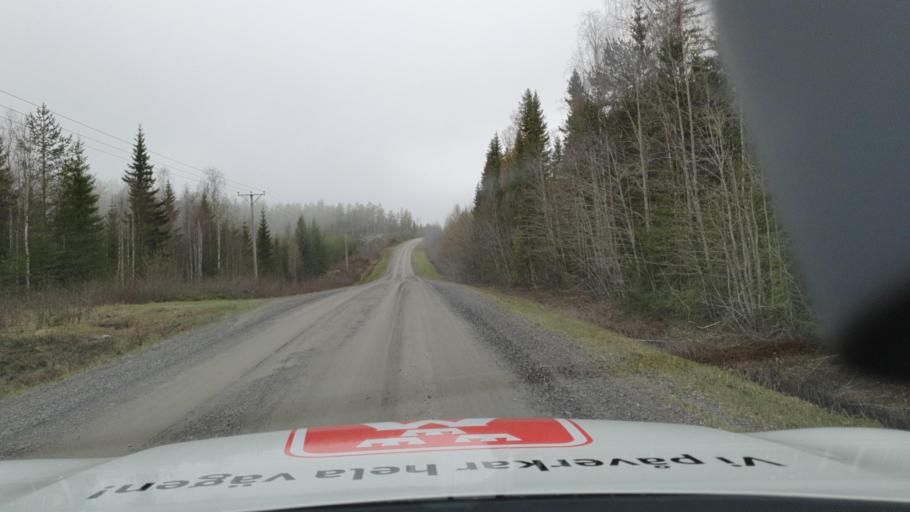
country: SE
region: Vaesterbotten
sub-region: Nordmalings Kommun
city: Nordmaling
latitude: 63.7653
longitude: 19.4664
